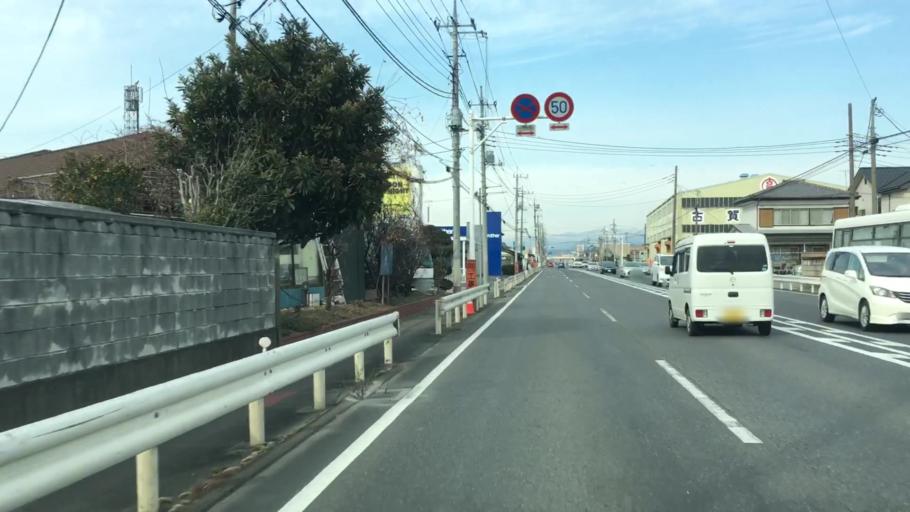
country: JP
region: Saitama
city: Menuma
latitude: 36.2500
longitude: 139.3789
